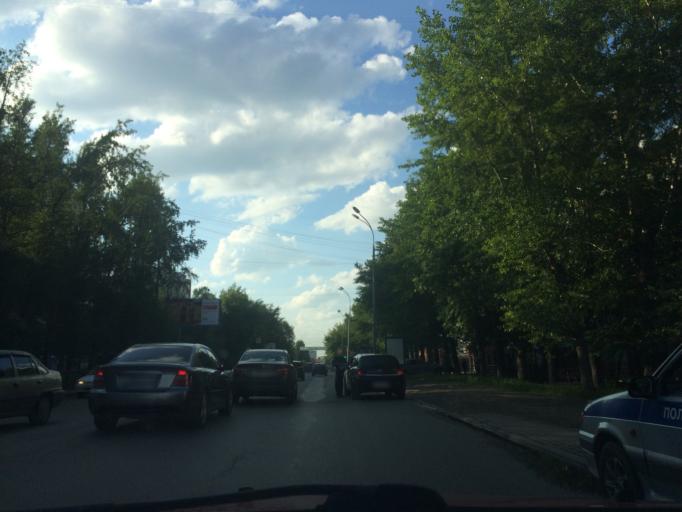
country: RU
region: Sverdlovsk
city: Yekaterinburg
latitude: 56.8278
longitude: 60.6373
